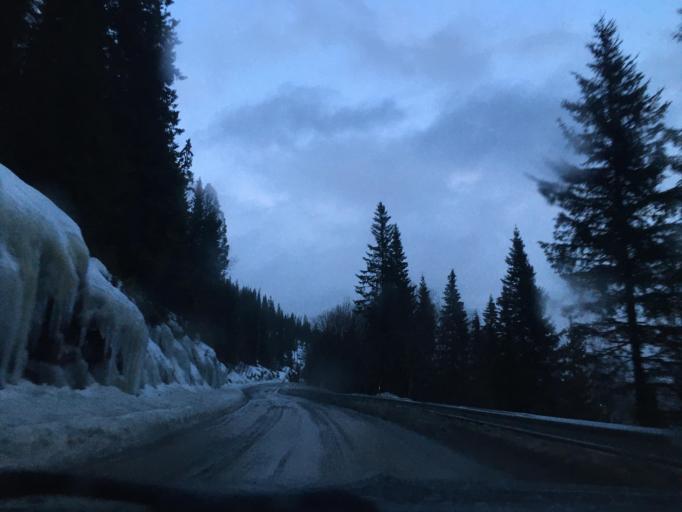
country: NO
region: Nordland
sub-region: Rana
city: Hauknes
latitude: 66.2946
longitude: 13.9184
